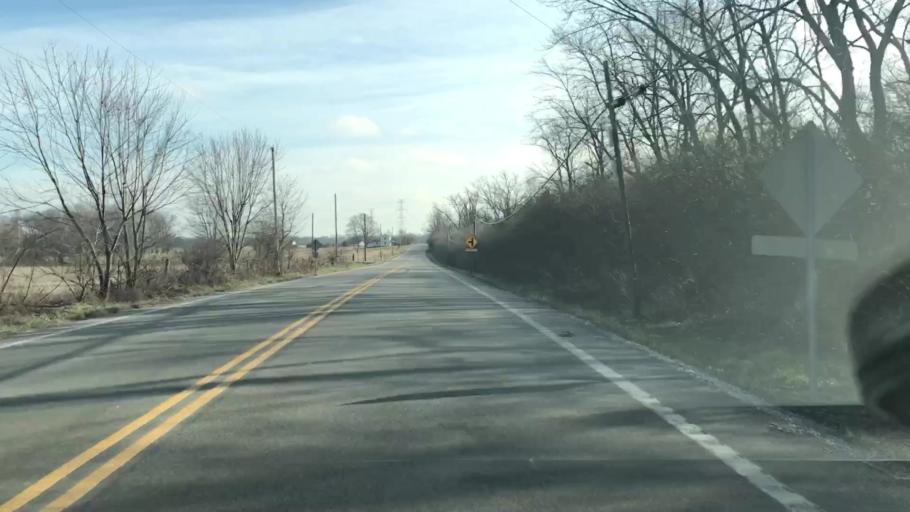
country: US
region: Ohio
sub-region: Greene County
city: Fairborn
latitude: 39.8100
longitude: -83.9794
